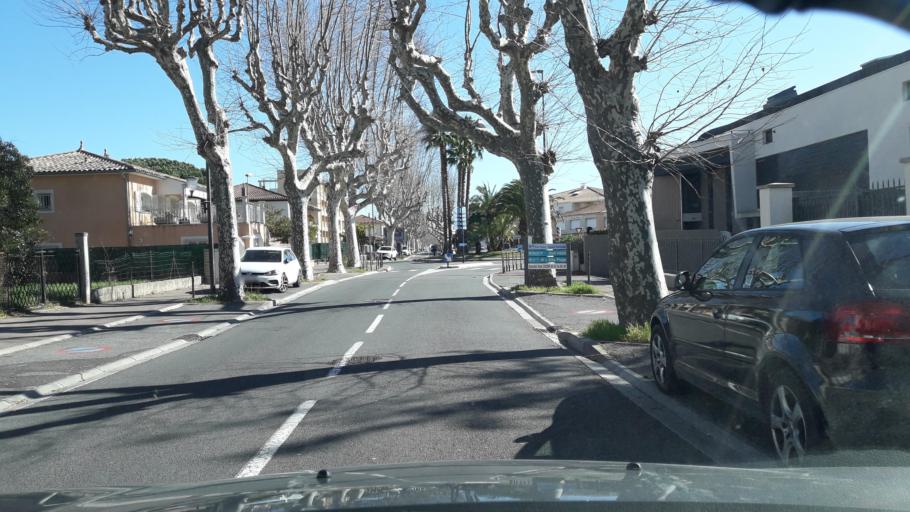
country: FR
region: Provence-Alpes-Cote d'Azur
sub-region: Departement du Var
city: Frejus
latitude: 43.4261
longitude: 6.7380
